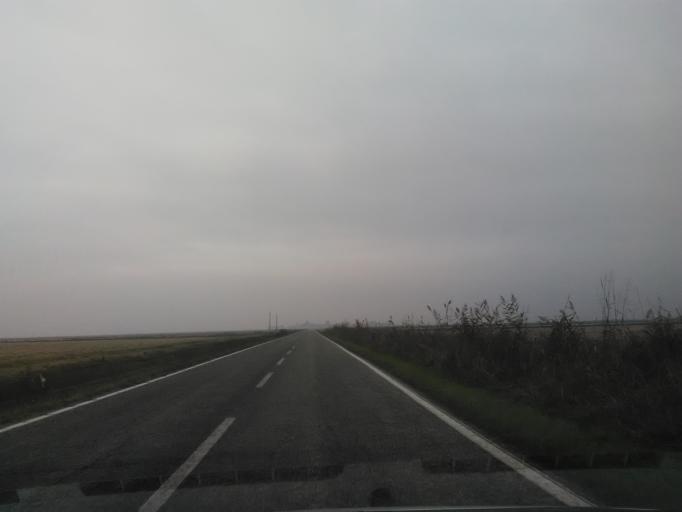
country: IT
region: Piedmont
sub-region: Provincia di Vercelli
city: Sali Vercellese
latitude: 45.2918
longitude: 8.3140
